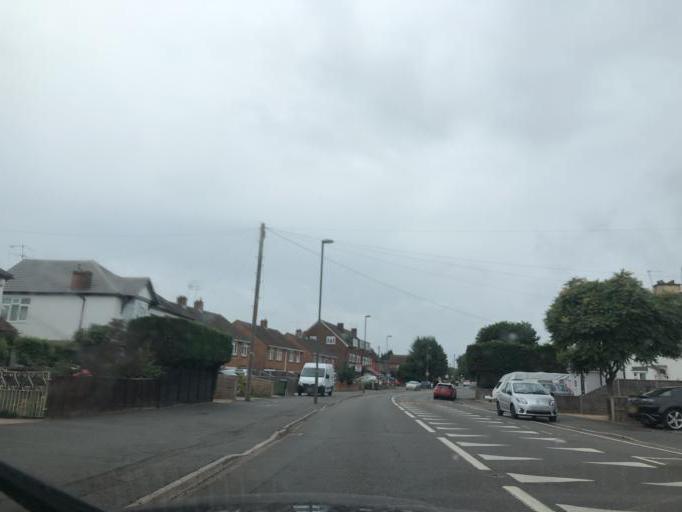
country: GB
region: England
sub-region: Surrey
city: Frimley
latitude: 51.2946
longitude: -0.7265
